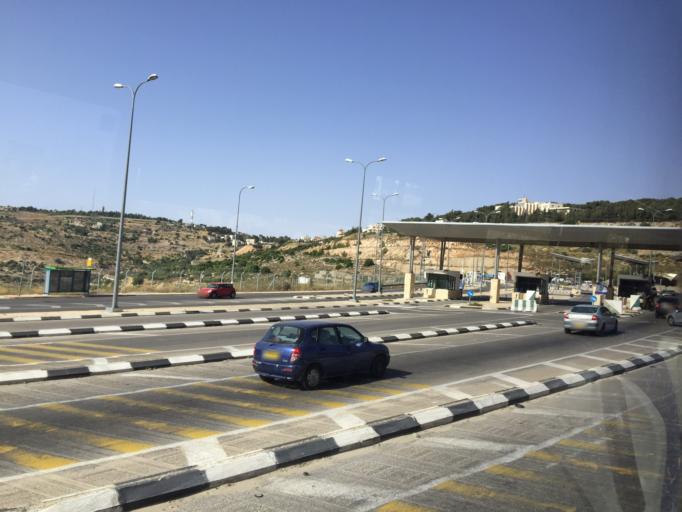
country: PS
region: West Bank
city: Al Khadir
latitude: 31.7052
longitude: 35.1682
